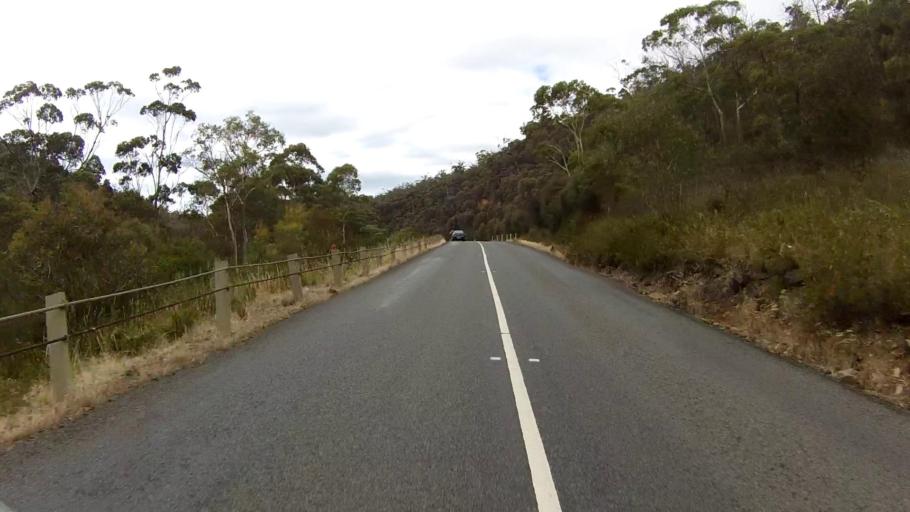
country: AU
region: Tasmania
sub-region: Sorell
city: Sorell
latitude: -42.5578
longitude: 147.8337
